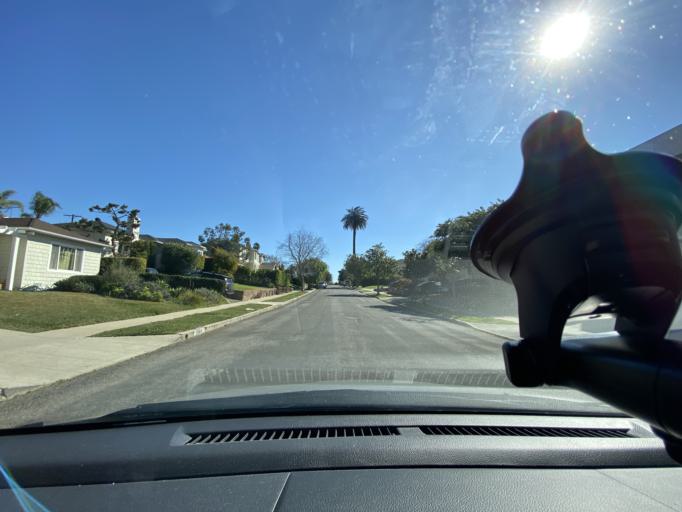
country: US
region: California
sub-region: Los Angeles County
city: Culver City
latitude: 34.0282
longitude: -118.4227
